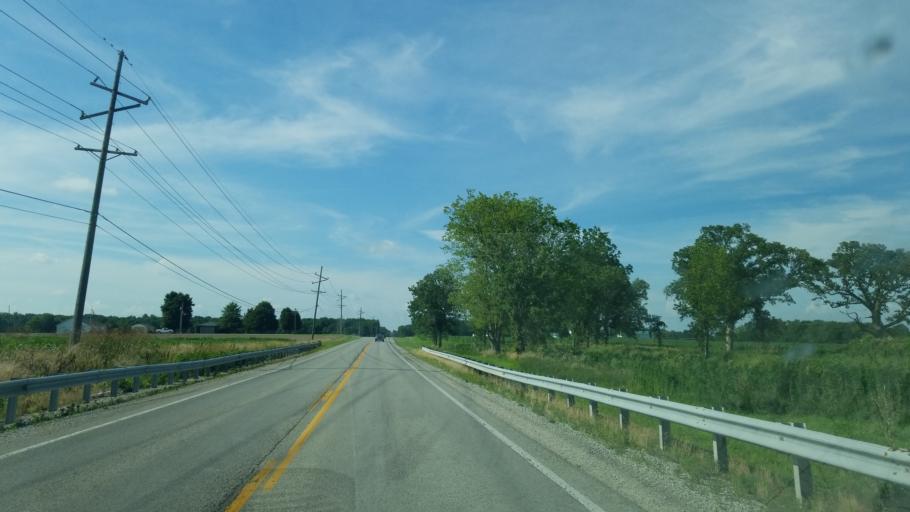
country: US
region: Illinois
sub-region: Saint Clair County
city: Lebanon
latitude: 38.5674
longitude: -89.8078
